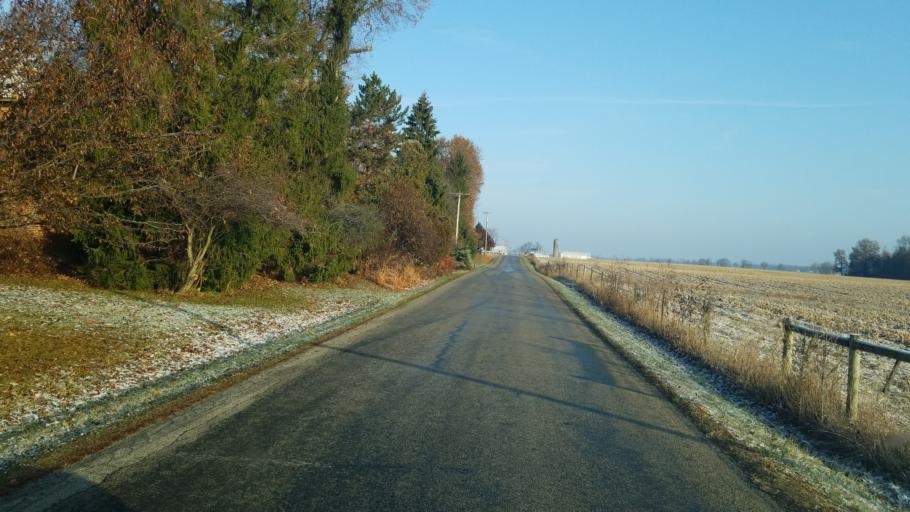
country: US
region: Ohio
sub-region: Crawford County
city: Bucyrus
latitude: 40.7619
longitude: -82.9013
